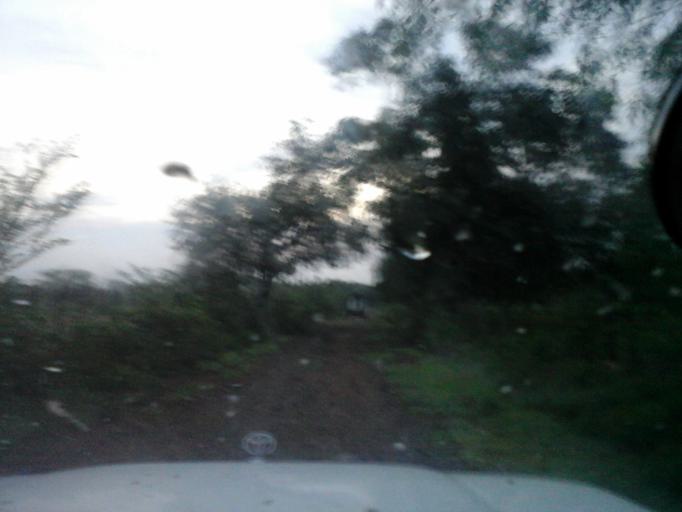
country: CO
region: Cesar
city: Agustin Codazzi
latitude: 10.1595
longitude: -73.2049
